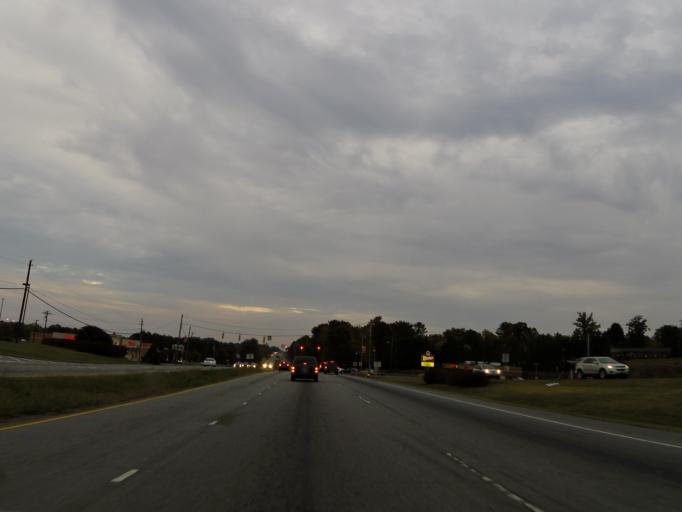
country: US
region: North Carolina
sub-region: Caldwell County
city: Hudson
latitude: 35.8472
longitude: -81.4753
